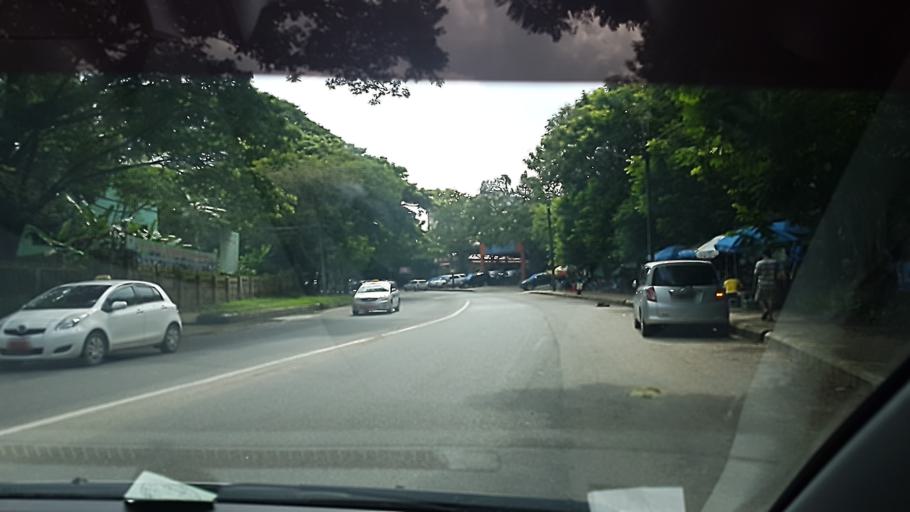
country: MM
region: Yangon
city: Yangon
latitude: 16.8075
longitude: 96.1514
